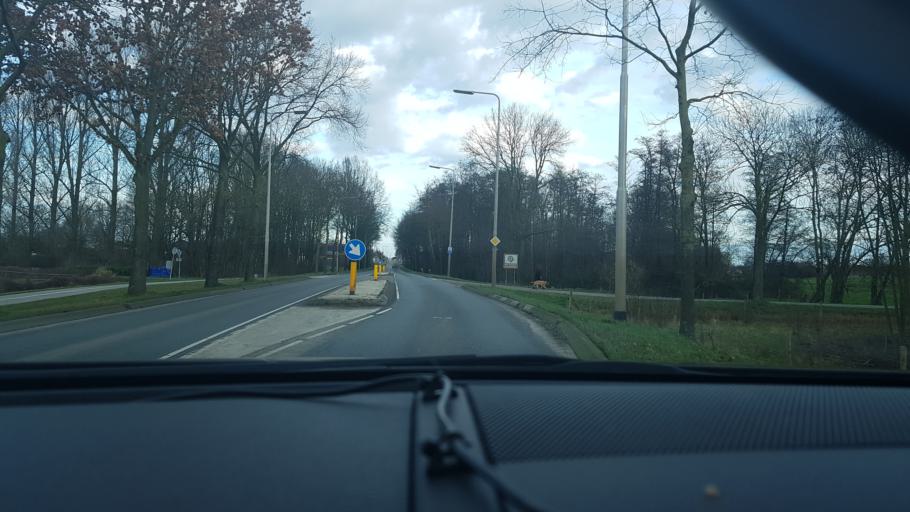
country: NL
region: Limburg
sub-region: Gemeente Leudal
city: Haelen
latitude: 51.2532
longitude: 5.9782
